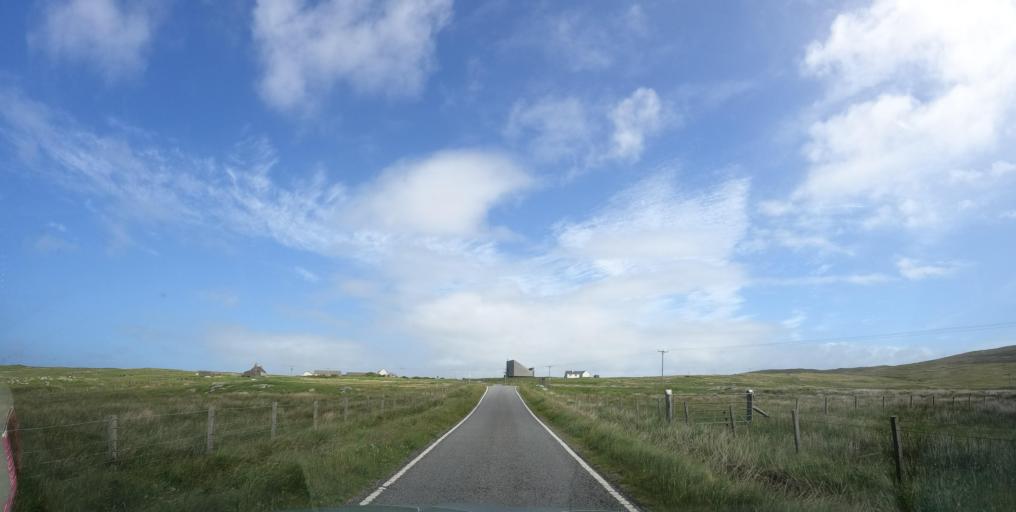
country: GB
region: Scotland
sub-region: Eilean Siar
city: Isle of South Uist
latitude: 57.1220
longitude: -7.3613
